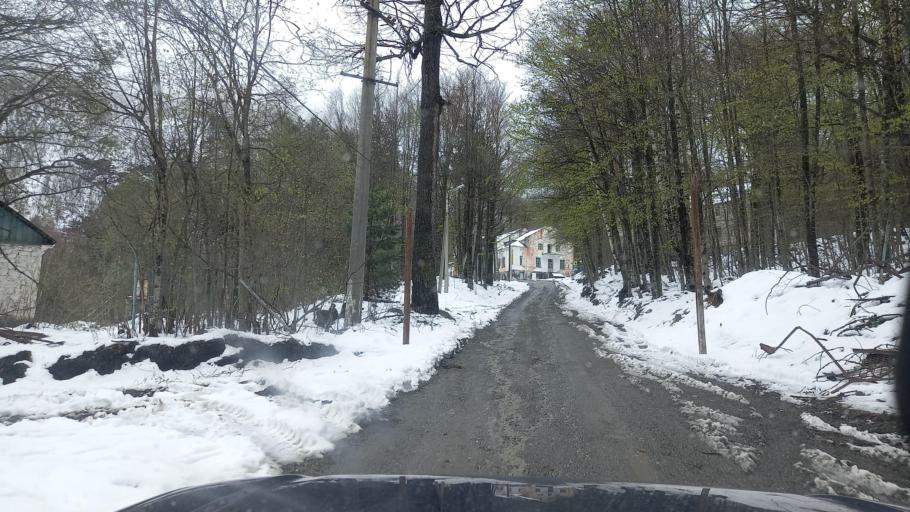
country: RU
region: North Ossetia
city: Mizur
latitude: 42.7879
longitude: 43.9030
